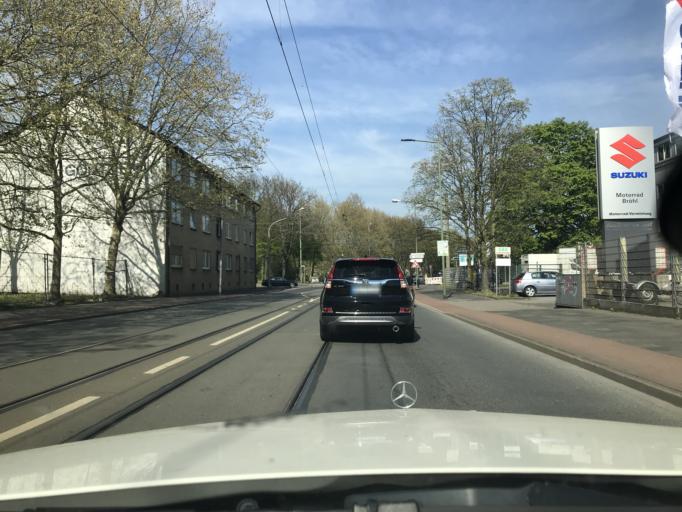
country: DE
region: North Rhine-Westphalia
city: Meiderich
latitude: 51.4782
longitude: 6.7910
